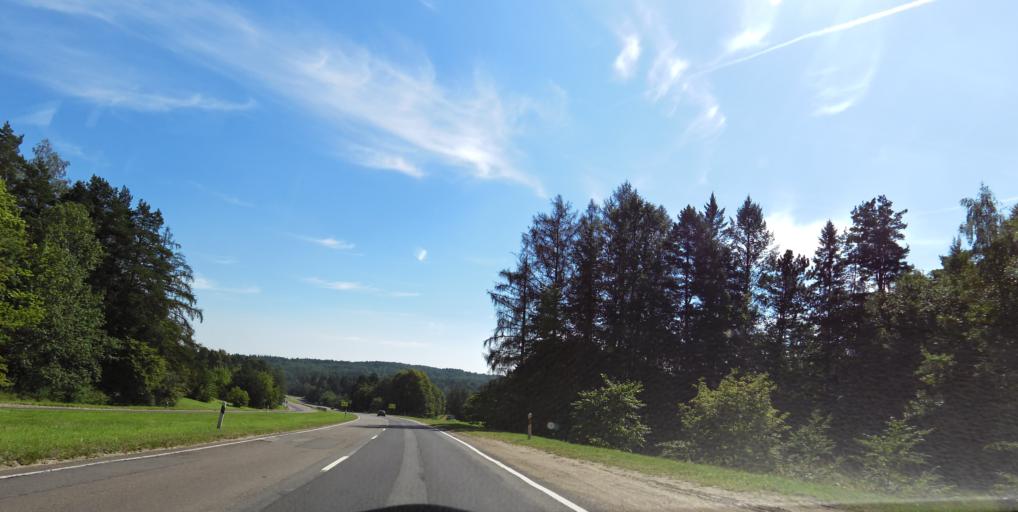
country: LT
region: Vilnius County
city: Rasos
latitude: 54.6923
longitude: 25.3563
